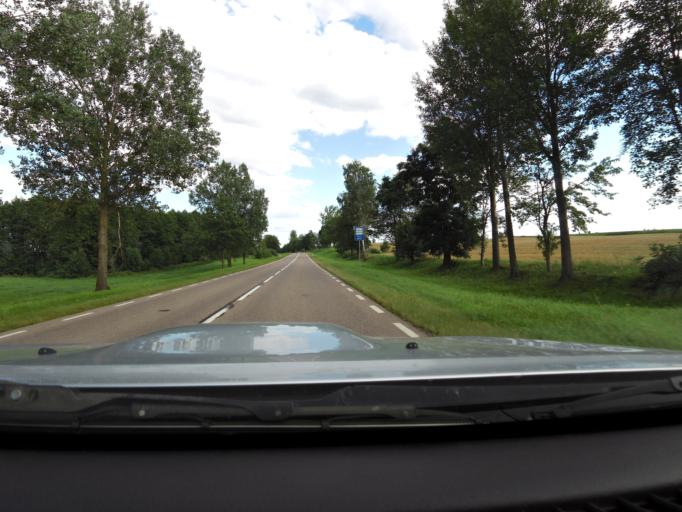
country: PL
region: Podlasie
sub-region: Powiat suwalski
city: Raczki
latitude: 53.8468
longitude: 22.7902
